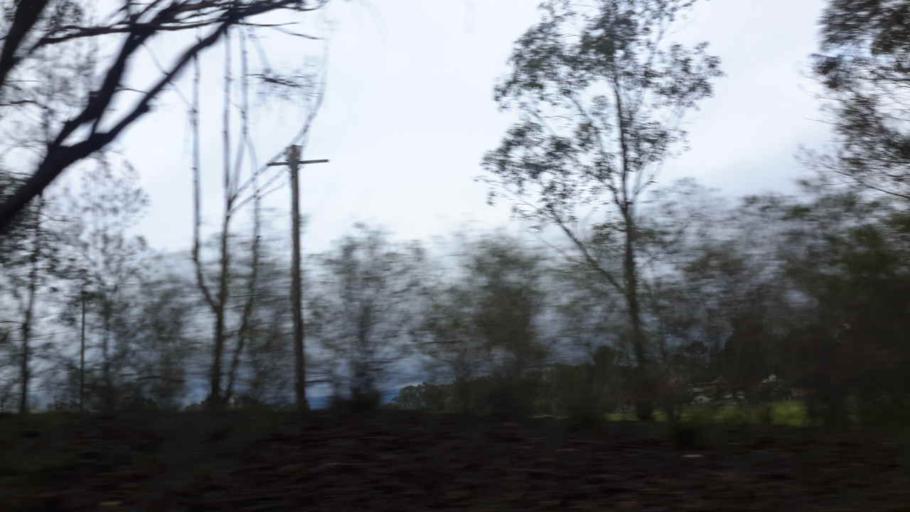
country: AU
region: New South Wales
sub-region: Penrith Municipality
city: Cambridge Park
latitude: -33.7488
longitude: 150.7138
